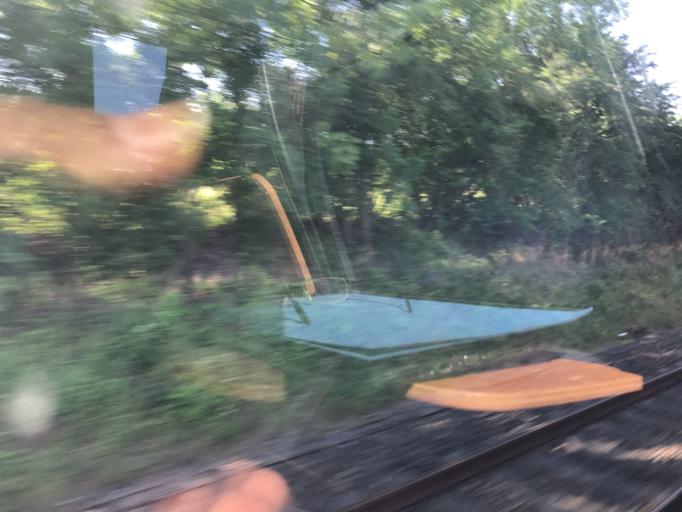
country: DE
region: Rheinland-Pfalz
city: Hintertiefenbach
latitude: 49.7107
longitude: 7.3634
